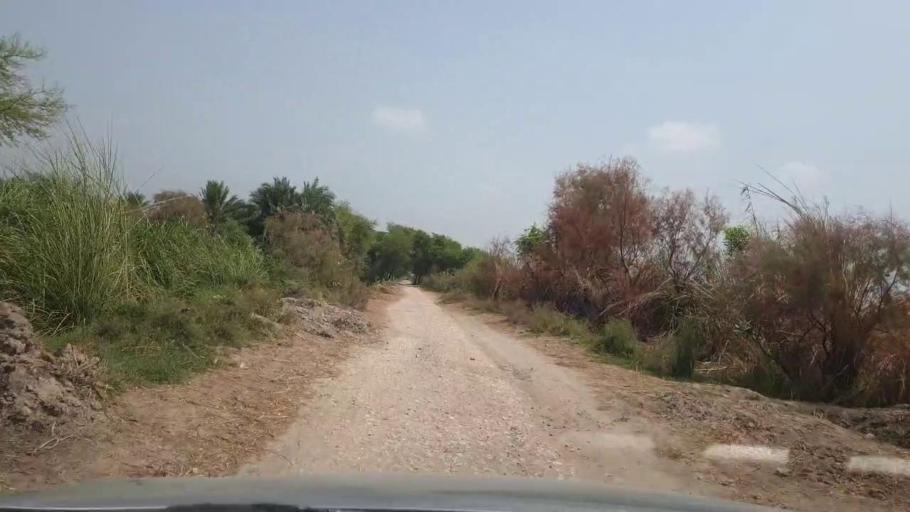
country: PK
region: Sindh
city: Garhi Yasin
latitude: 27.9360
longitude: 68.3670
